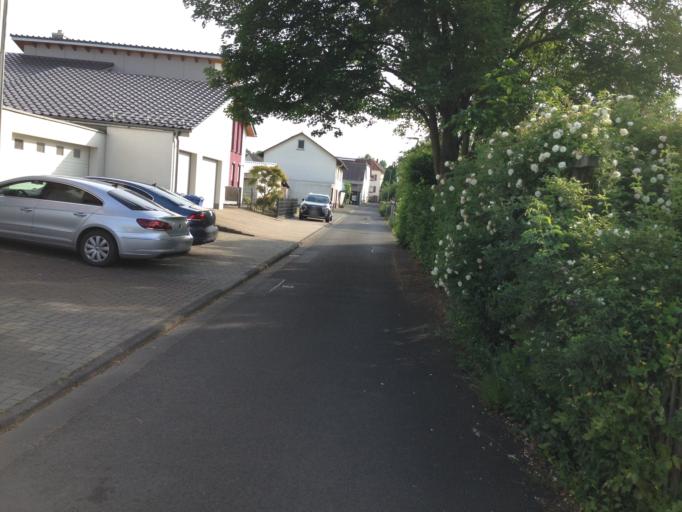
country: DE
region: Hesse
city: Allendorf an der Lahn
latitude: 50.5505
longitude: 8.6191
